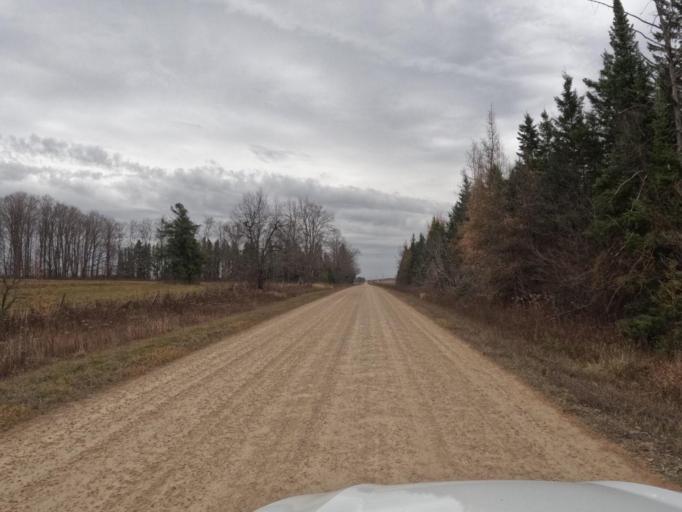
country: CA
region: Ontario
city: Shelburne
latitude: 44.0244
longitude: -80.3927
